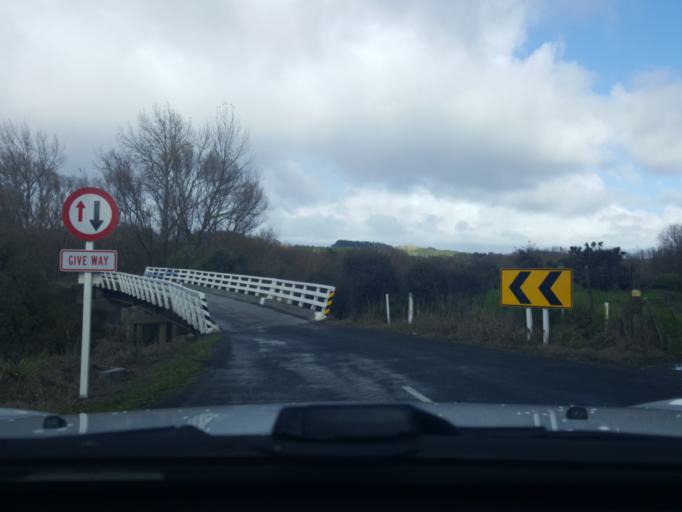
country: NZ
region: Waikato
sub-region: Waikato District
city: Te Kauwhata
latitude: -37.4093
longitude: 175.0587
